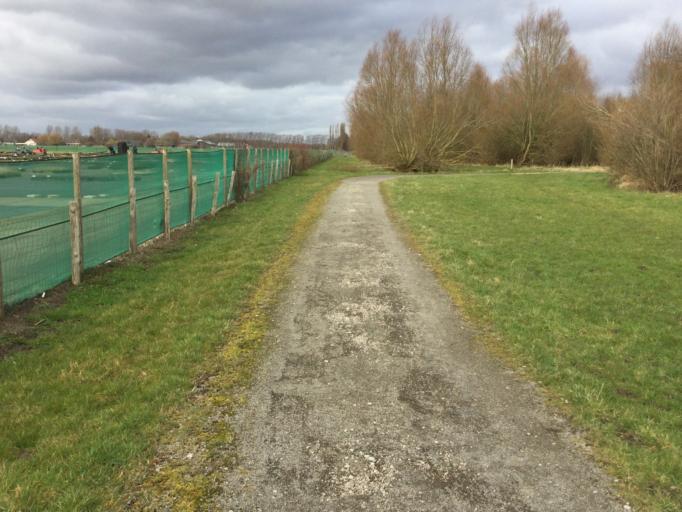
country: NL
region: South Holland
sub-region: Gemeente Hillegom
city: Hillegom
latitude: 52.2939
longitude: 4.6026
